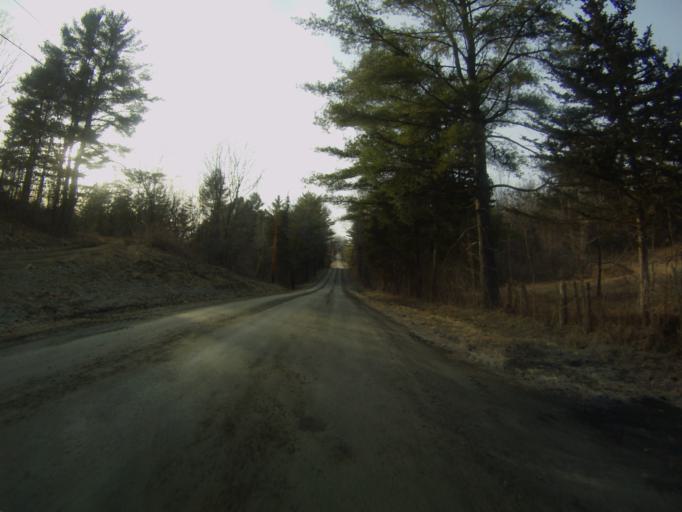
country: US
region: Vermont
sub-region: Addison County
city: Middlebury (village)
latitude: 44.0382
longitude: -73.2759
